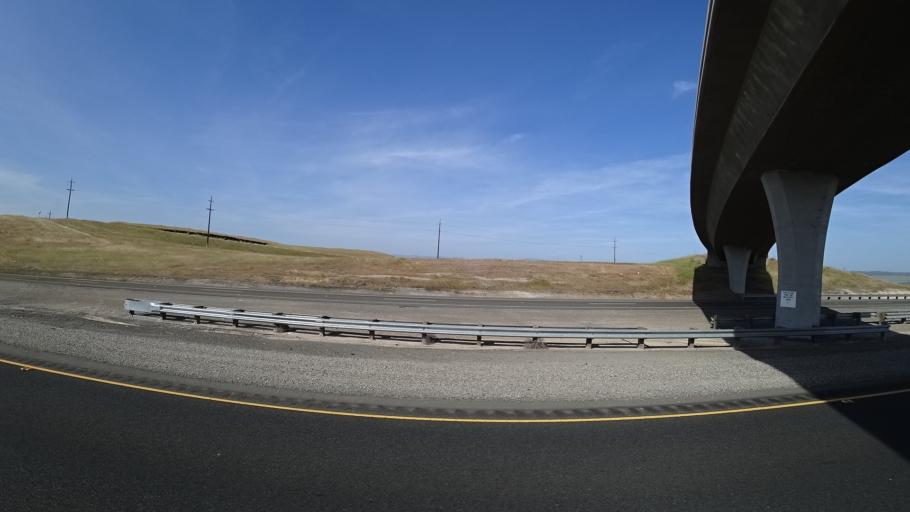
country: US
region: California
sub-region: Butte County
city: Durham
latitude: 39.6209
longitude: -121.6919
